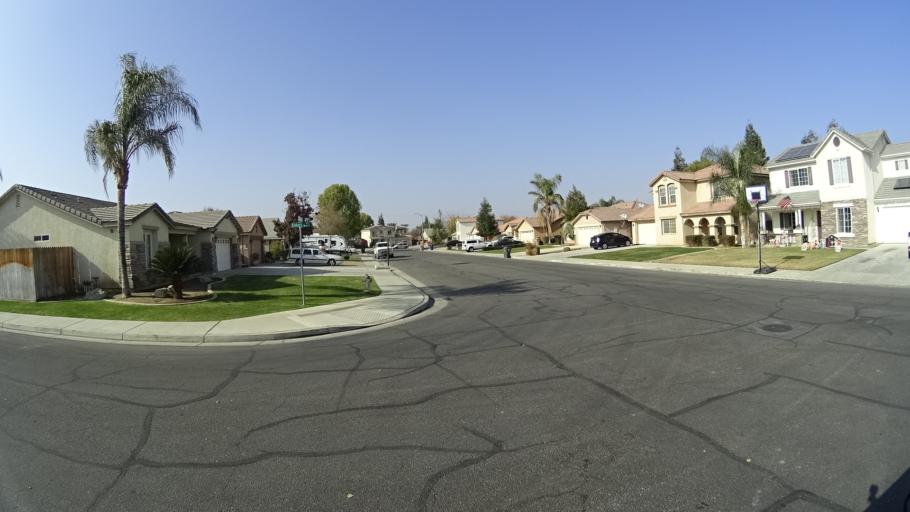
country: US
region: California
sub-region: Kern County
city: Greenacres
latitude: 35.4159
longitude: -119.1257
